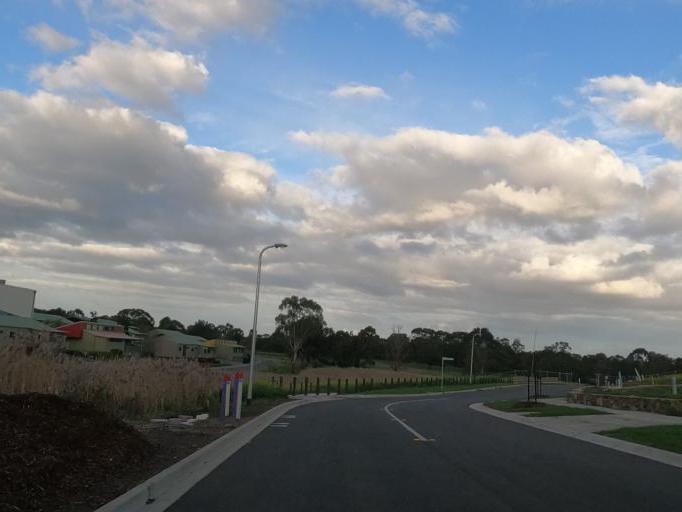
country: AU
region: Victoria
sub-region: Hume
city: Greenvale
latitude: -37.6285
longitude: 144.8890
